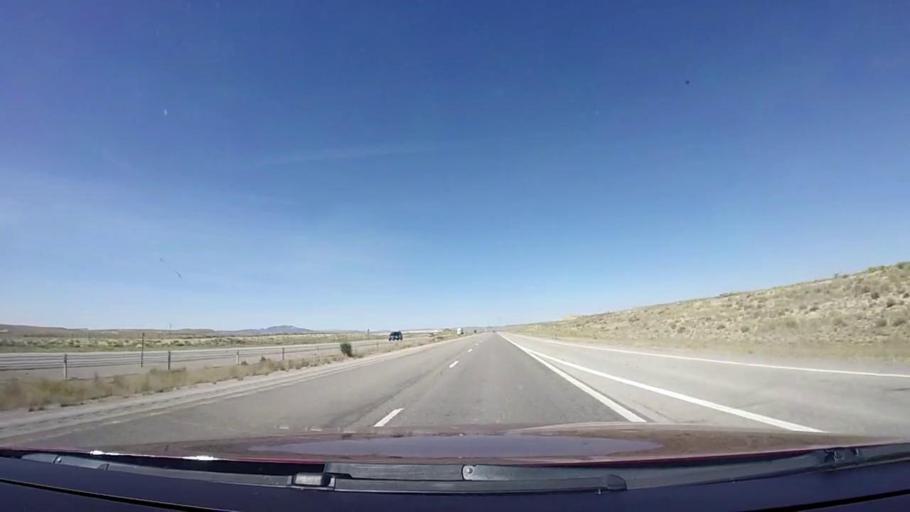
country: US
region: Wyoming
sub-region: Sweetwater County
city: Rock Springs
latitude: 41.6482
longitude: -108.6345
